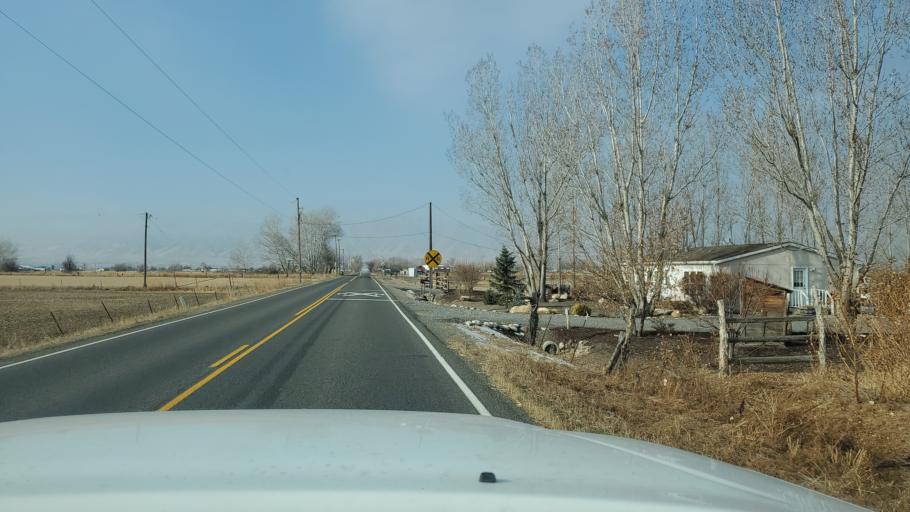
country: US
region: Utah
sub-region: Utah County
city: Benjamin
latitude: 40.0854
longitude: -111.7178
